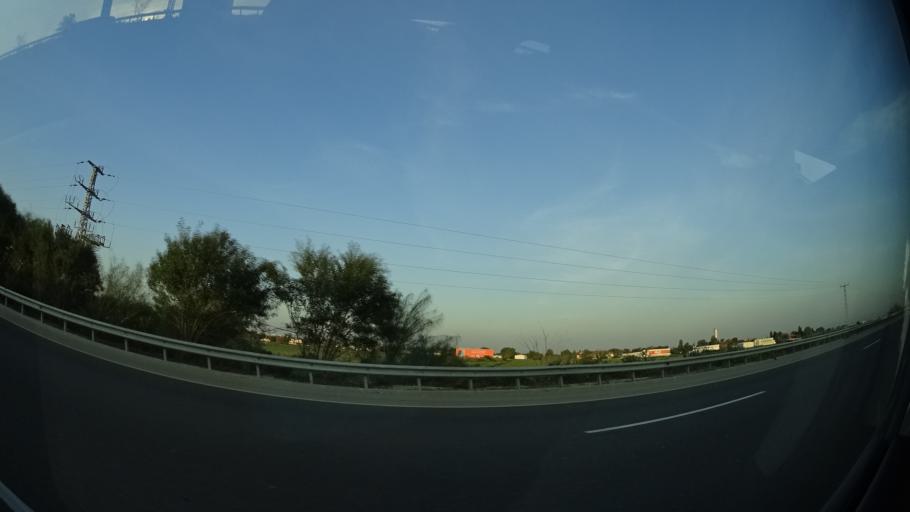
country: IL
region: Central District
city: Kefar Habad
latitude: 31.9980
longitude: 34.8503
